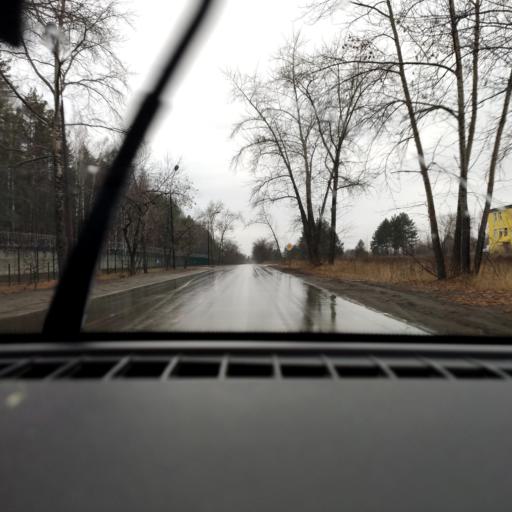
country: RU
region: Perm
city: Overyata
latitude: 57.9941
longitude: 55.9134
